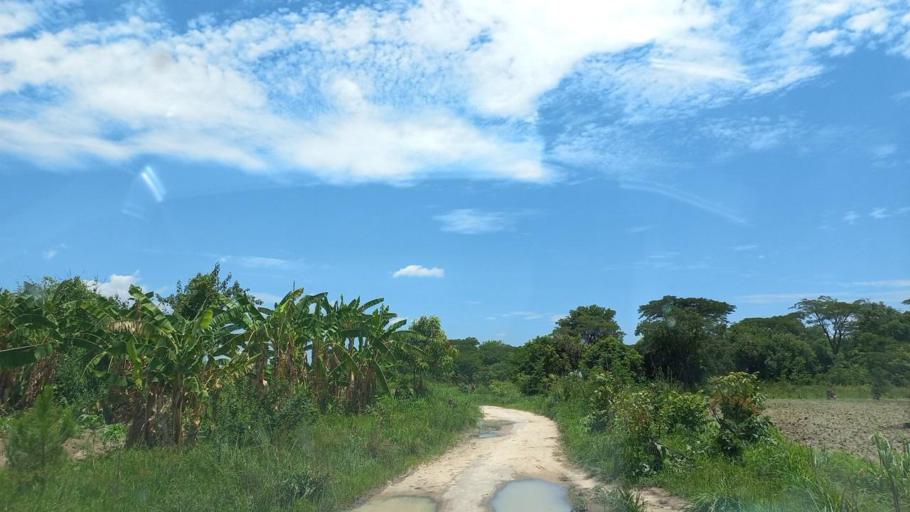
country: ZM
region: Copperbelt
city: Ndola
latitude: -12.8688
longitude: 28.4407
